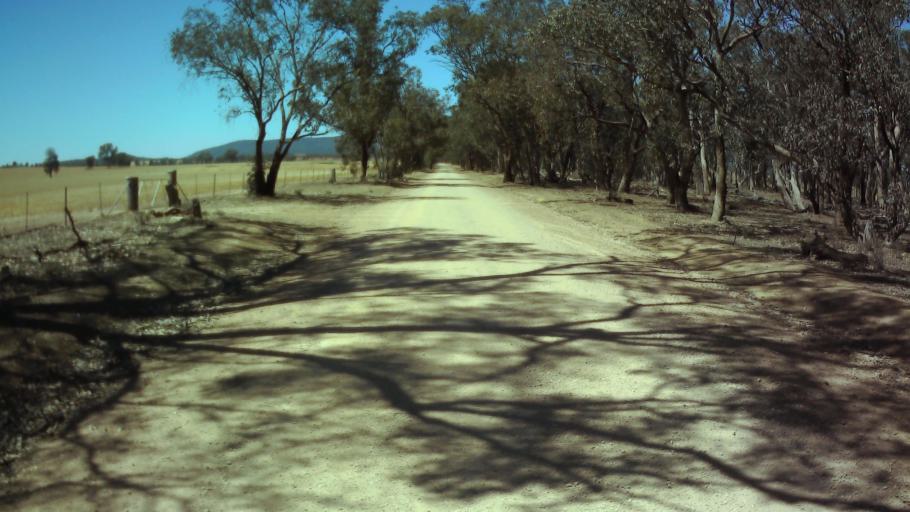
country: AU
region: New South Wales
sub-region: Weddin
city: Grenfell
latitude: -33.9128
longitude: 148.0797
